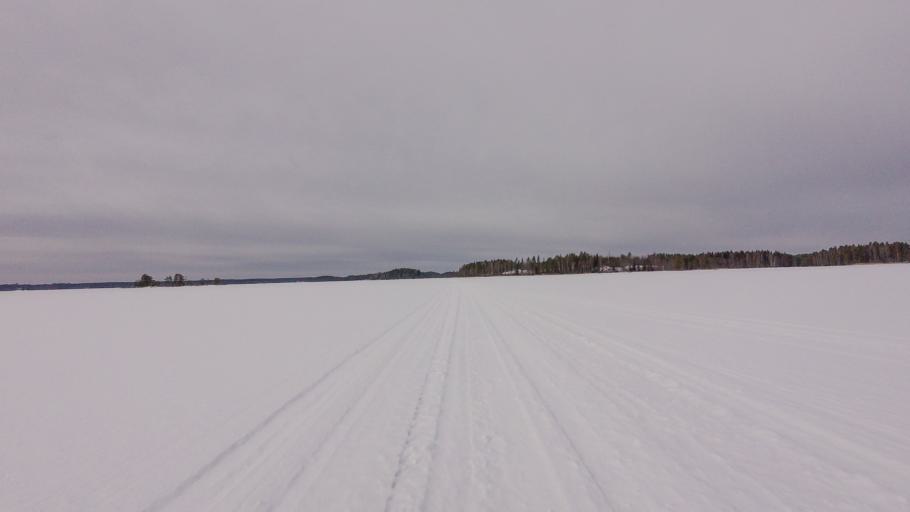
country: FI
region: Southern Savonia
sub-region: Savonlinna
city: Rantasalmi
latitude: 62.1146
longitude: 28.3535
